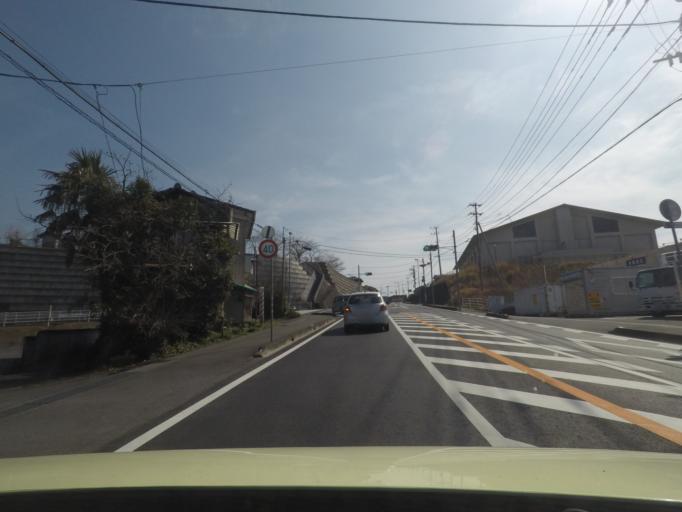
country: JP
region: Ibaraki
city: Ishioka
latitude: 36.1692
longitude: 140.3583
